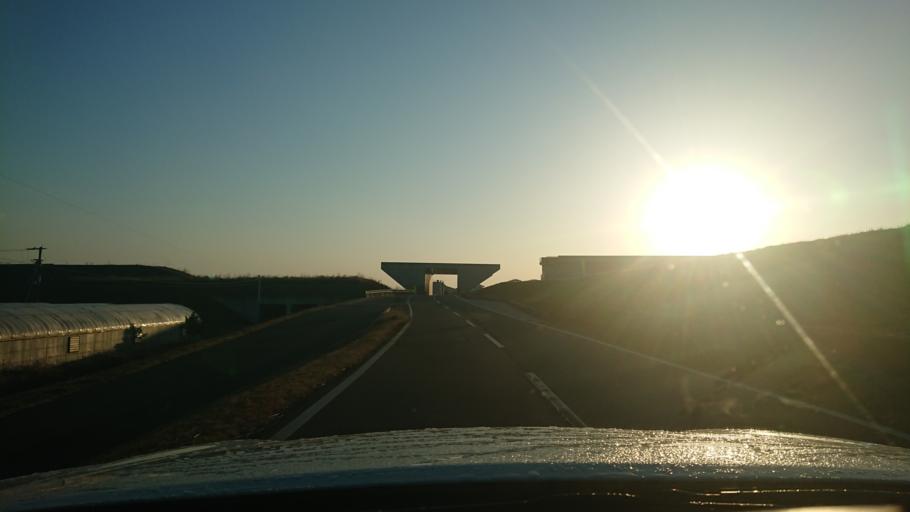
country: JP
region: Tokushima
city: Anan
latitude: 33.9412
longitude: 134.6092
